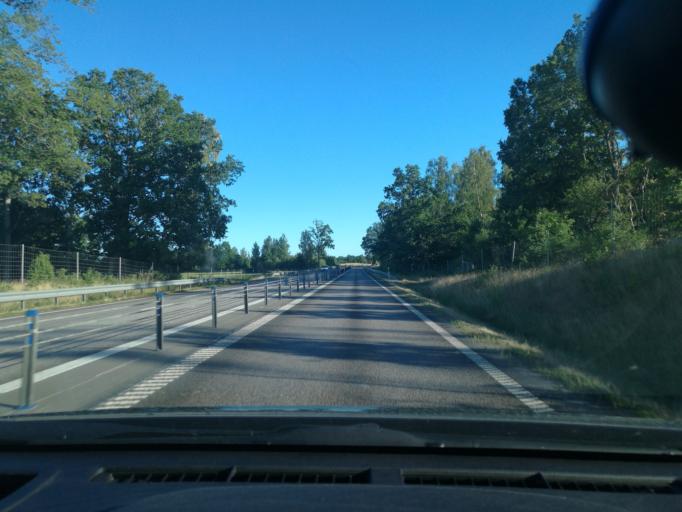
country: SE
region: Kalmar
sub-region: Monsteras Kommun
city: Timmernabben
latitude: 56.9224
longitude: 16.3855
